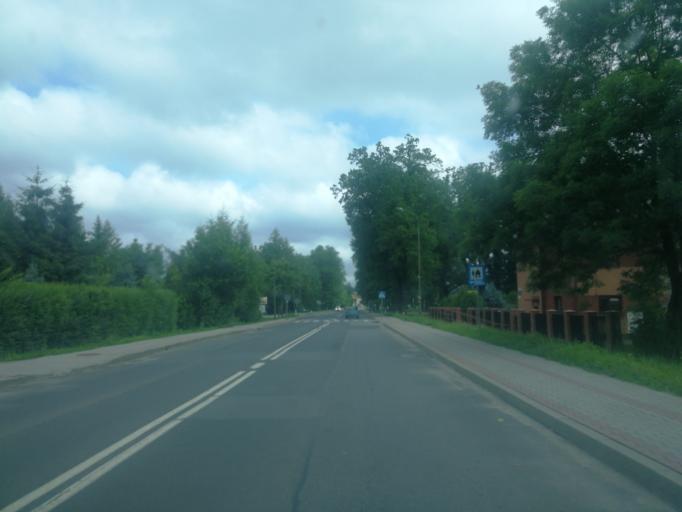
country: PL
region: Subcarpathian Voivodeship
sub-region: Powiat leski
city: Lesko
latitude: 49.4771
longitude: 22.3244
